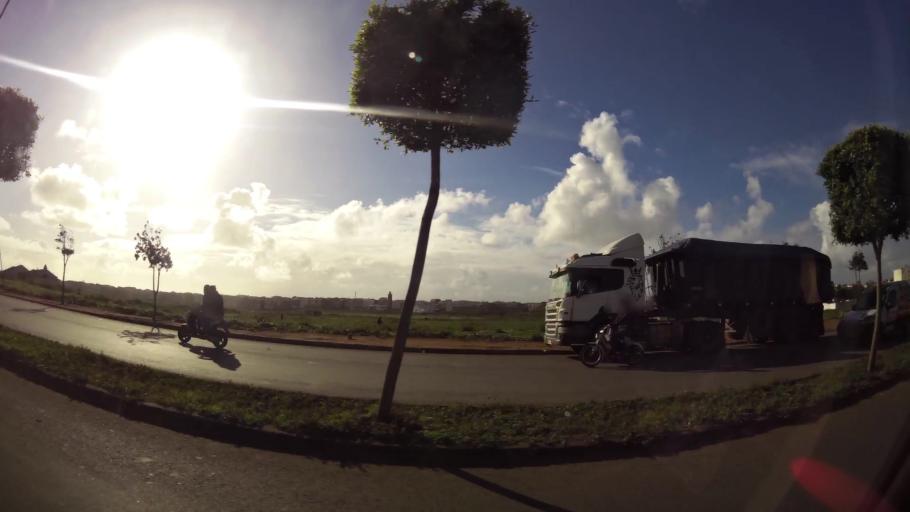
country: MA
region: Grand Casablanca
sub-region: Casablanca
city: Casablanca
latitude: 33.5612
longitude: -7.6848
